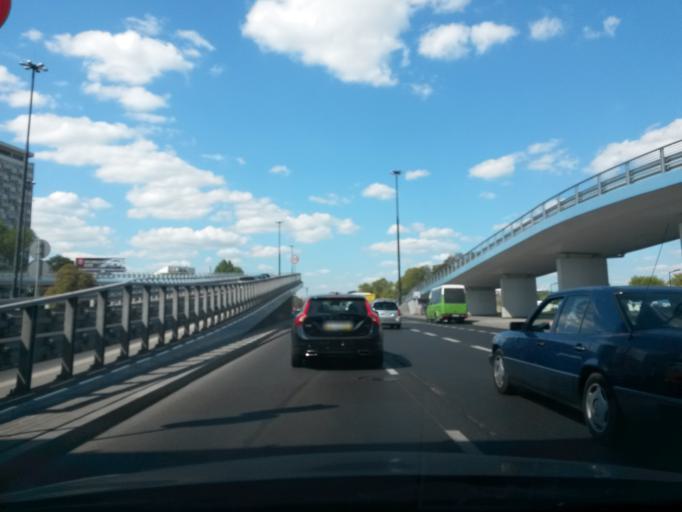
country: PL
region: Masovian Voivodeship
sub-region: Warszawa
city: Srodmiescie
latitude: 52.2244
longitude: 21.0439
